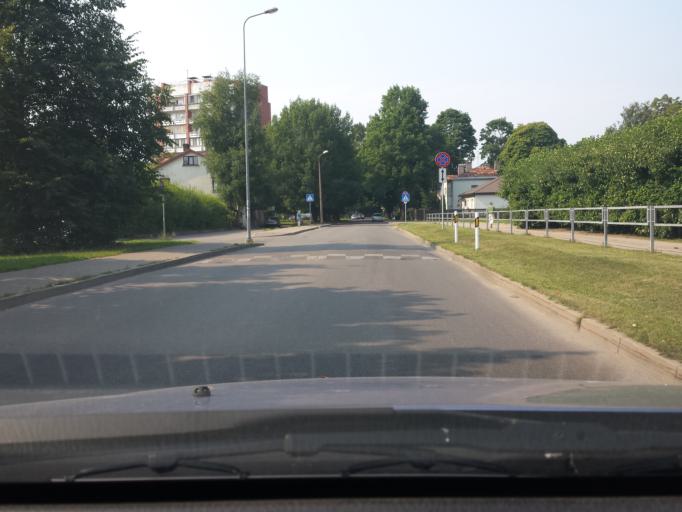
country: LV
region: Riga
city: Jaunciems
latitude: 56.9605
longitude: 24.1847
